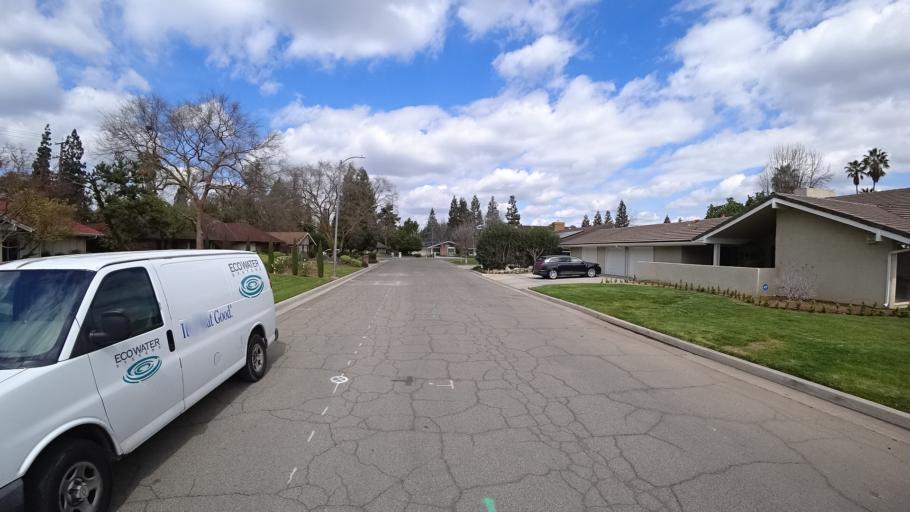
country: US
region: California
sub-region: Fresno County
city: Fresno
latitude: 36.8324
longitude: -119.8437
